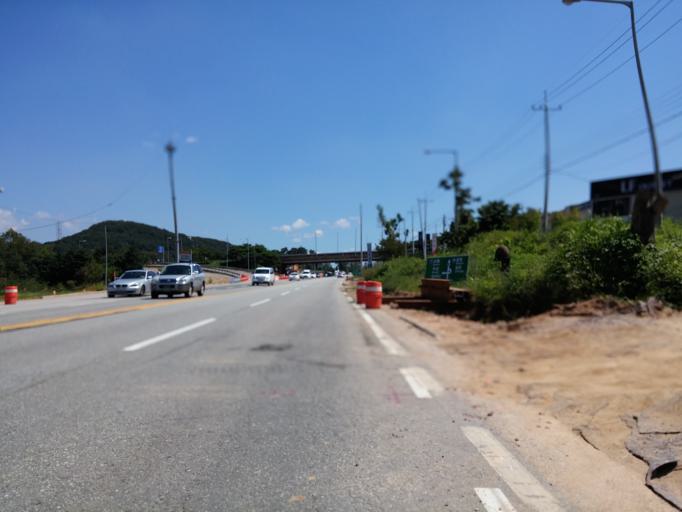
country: KR
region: Chungcheongbuk-do
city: Cheongju-si
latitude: 36.6234
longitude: 127.3752
